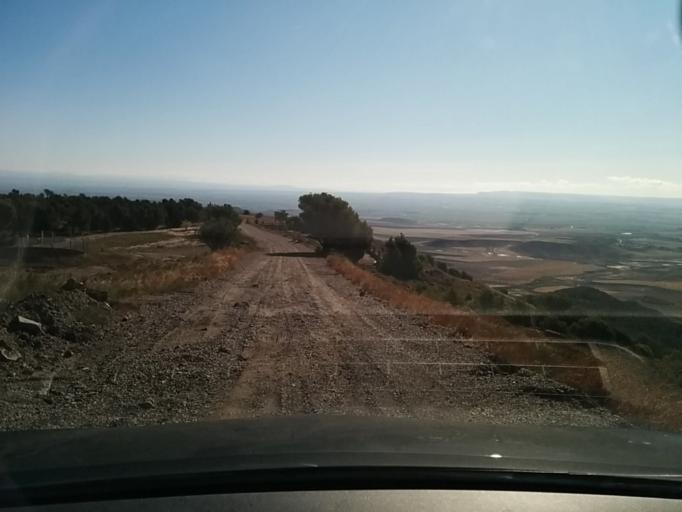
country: ES
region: Aragon
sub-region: Provincia de Zaragoza
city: Novillas
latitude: 42.0205
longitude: -1.3225
